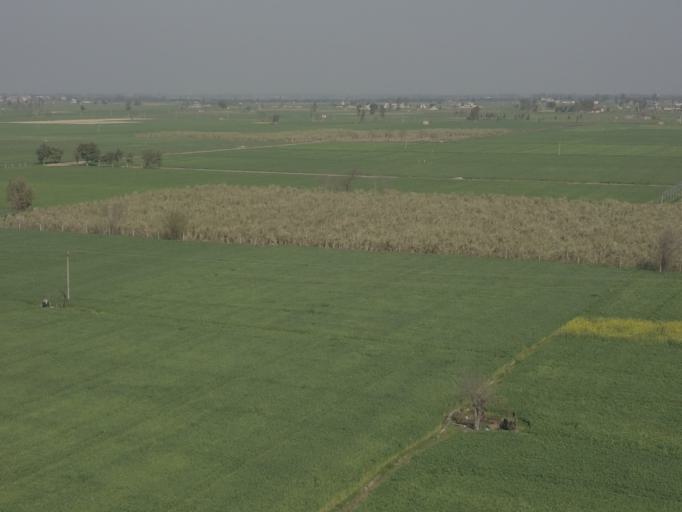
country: IN
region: Punjab
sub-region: Shahid Bhagat Singh Nagar
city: Rahon
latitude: 31.0231
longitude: 76.0894
